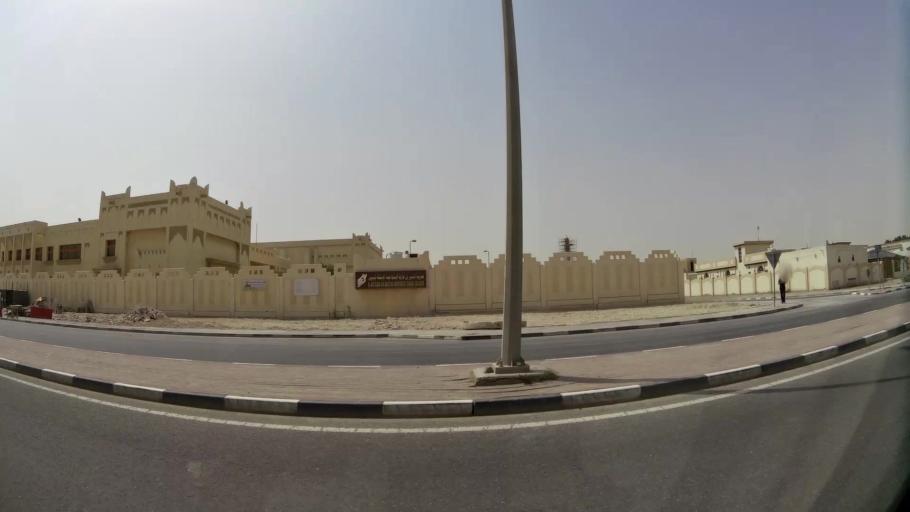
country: QA
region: Baladiyat ar Rayyan
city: Ar Rayyan
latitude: 25.2352
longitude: 51.4204
